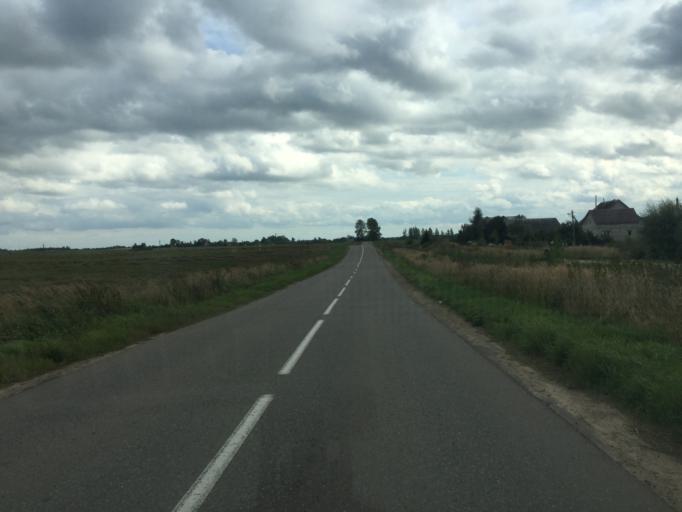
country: BY
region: Vitebsk
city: Vitebsk
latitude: 55.1562
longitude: 30.2679
